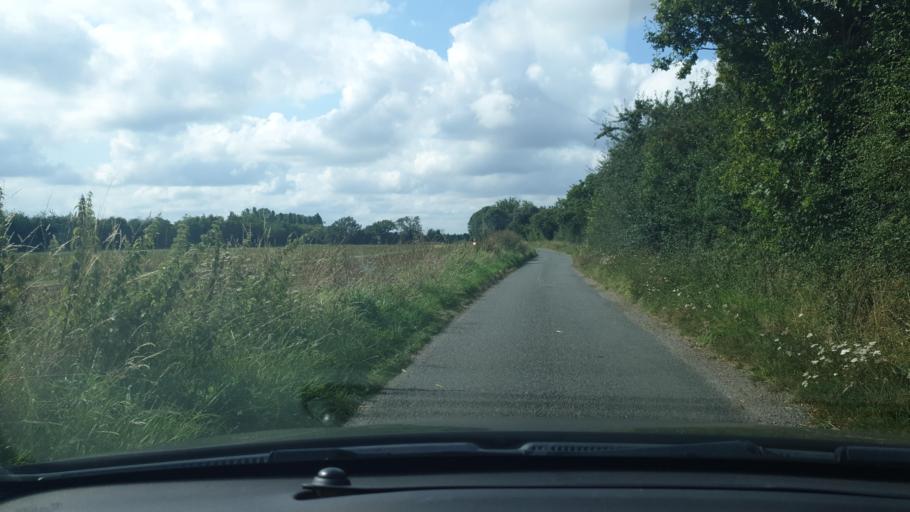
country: GB
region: England
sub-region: Essex
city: Manningtree
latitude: 51.9181
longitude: 1.0166
